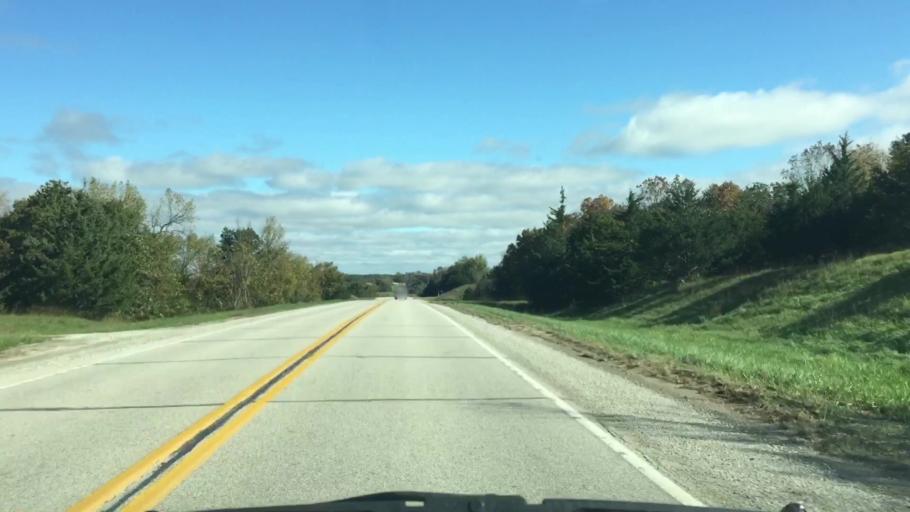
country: US
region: Iowa
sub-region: Decatur County
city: Leon
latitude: 40.6729
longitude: -93.7881
